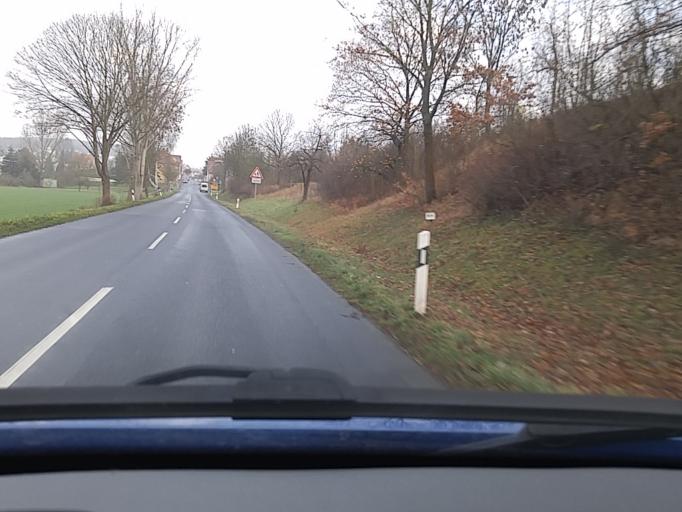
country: DE
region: Hesse
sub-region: Regierungsbezirk Darmstadt
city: Bad Nauheim
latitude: 50.3716
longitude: 8.7653
